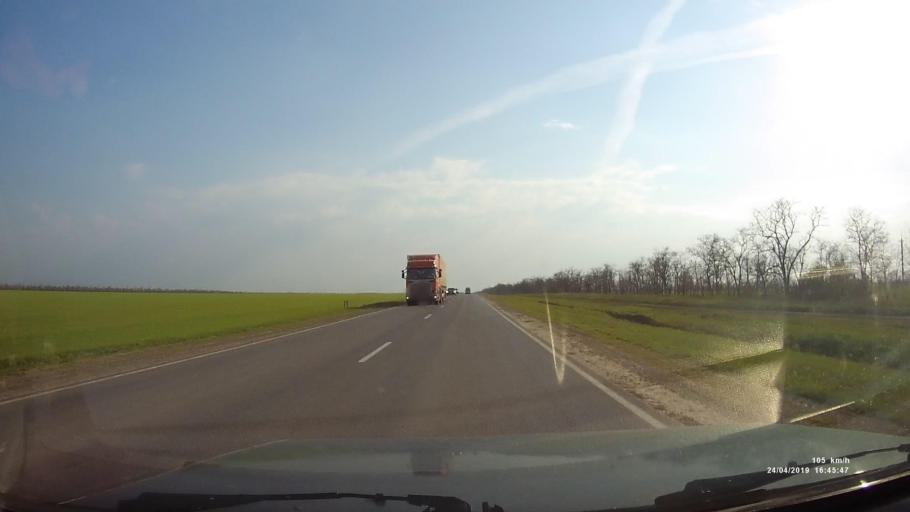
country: RU
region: Rostov
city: Gundorovskiy
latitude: 46.7650
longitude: 41.8099
